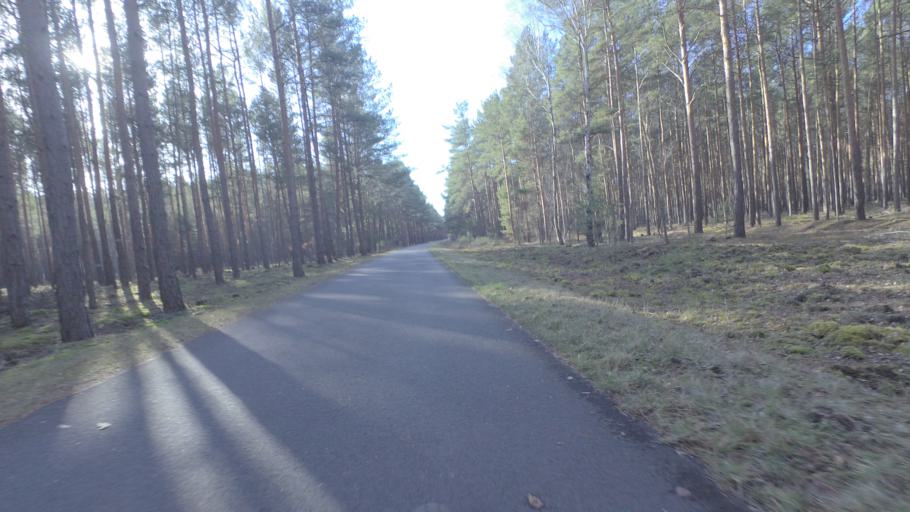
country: DE
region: Brandenburg
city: Luckenwalde
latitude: 52.0525
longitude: 13.1506
